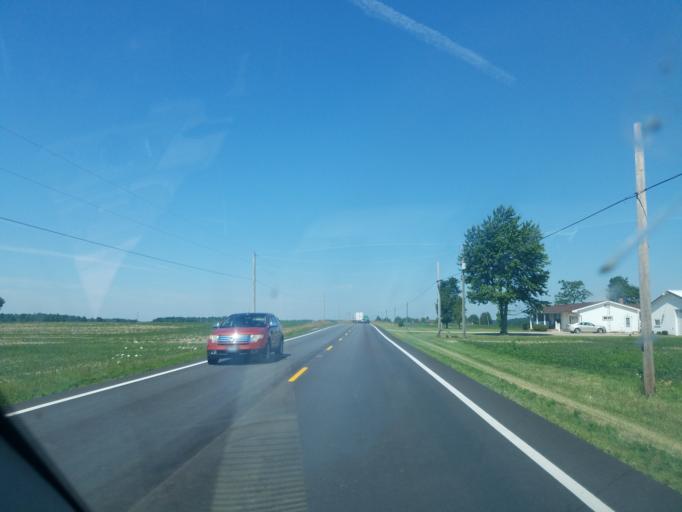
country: US
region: Ohio
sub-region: Shelby County
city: Botkins
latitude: 40.4392
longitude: -84.1160
